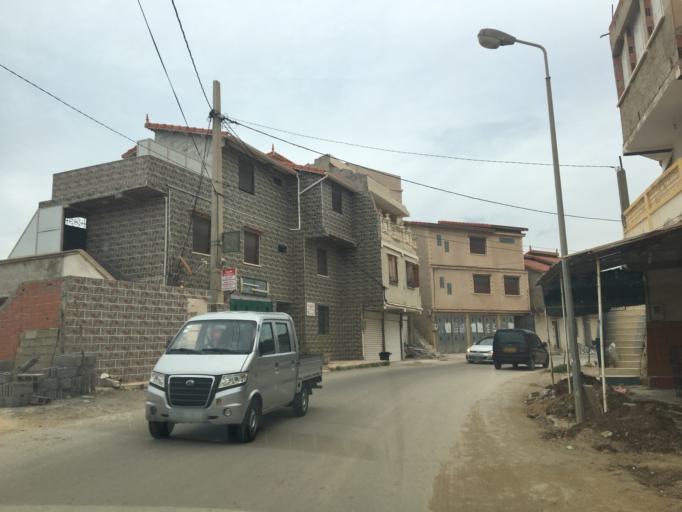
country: DZ
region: Tipaza
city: Tipasa
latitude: 36.6415
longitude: 2.3608
